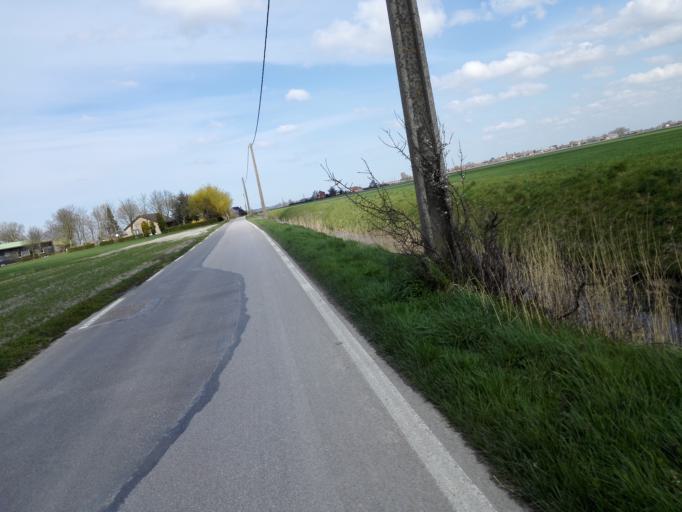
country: FR
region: Nord-Pas-de-Calais
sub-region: Departement du Nord
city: Brouckerque
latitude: 50.9615
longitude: 2.2998
